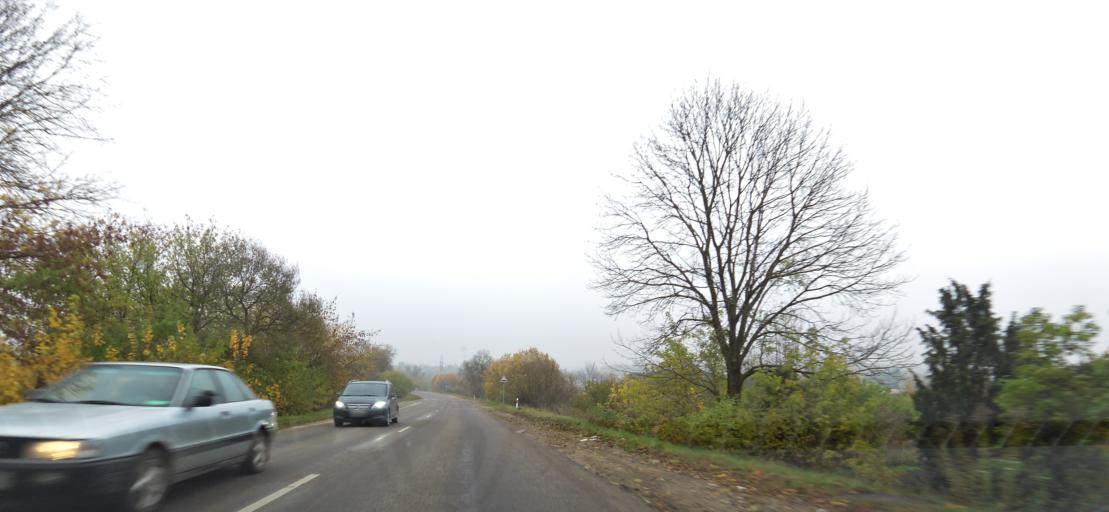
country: LT
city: Skaidiskes
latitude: 54.6578
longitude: 25.3727
